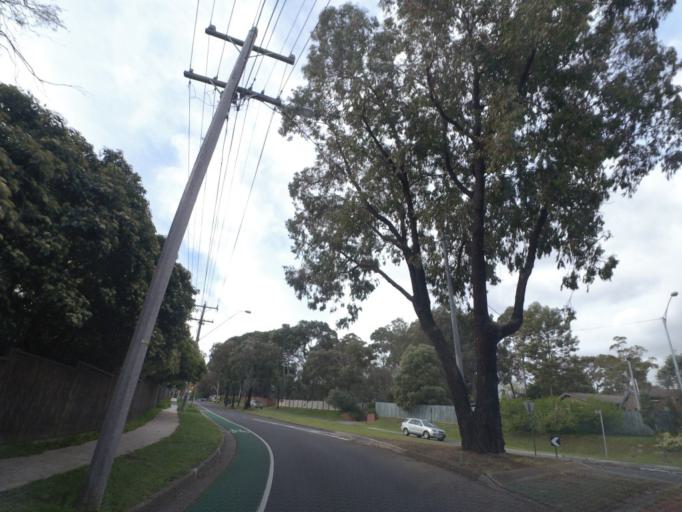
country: AU
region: Victoria
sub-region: Whitehorse
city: Vermont South
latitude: -37.8509
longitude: 145.1882
